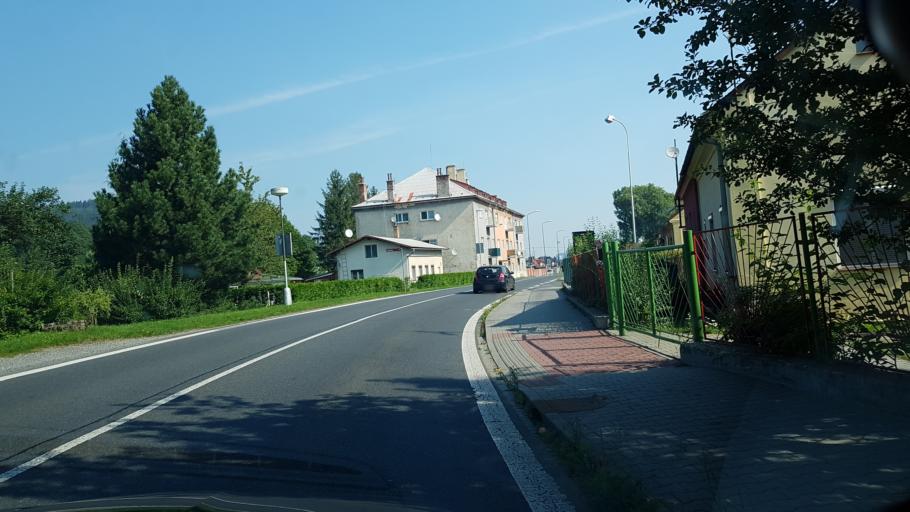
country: CZ
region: Olomoucky
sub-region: Okres Jesenik
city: Jesenik
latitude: 50.2385
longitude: 17.2065
